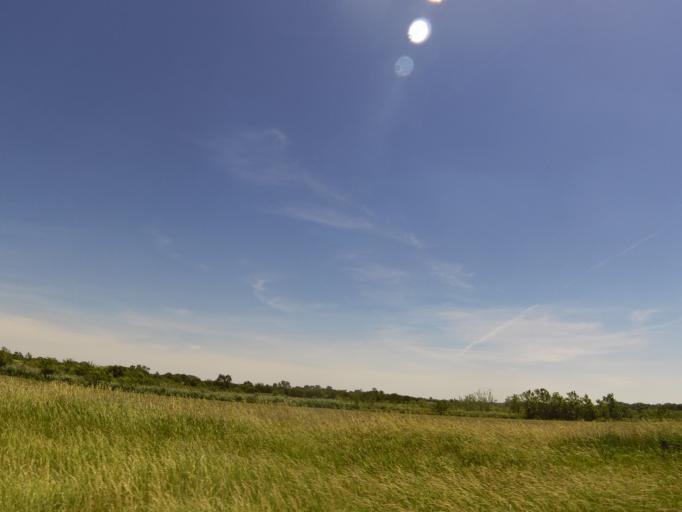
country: US
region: Illinois
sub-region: Vermilion County
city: Hoopeston
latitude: 40.4510
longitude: -87.6868
